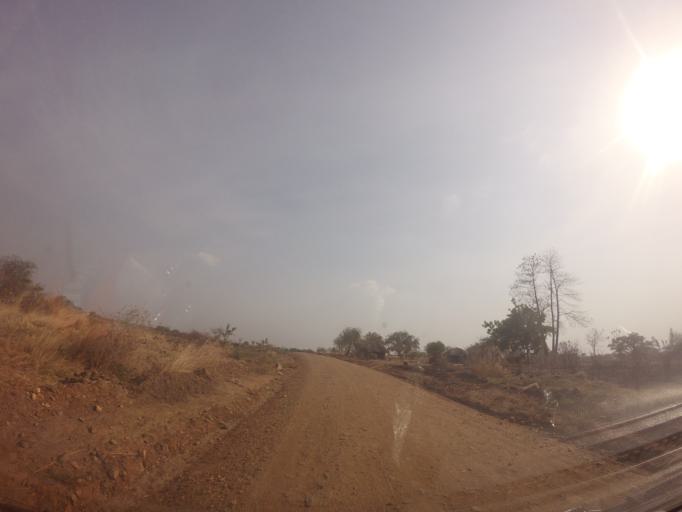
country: UG
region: Northern Region
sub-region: Maracha District
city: Maracha
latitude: 3.1040
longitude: 31.2125
